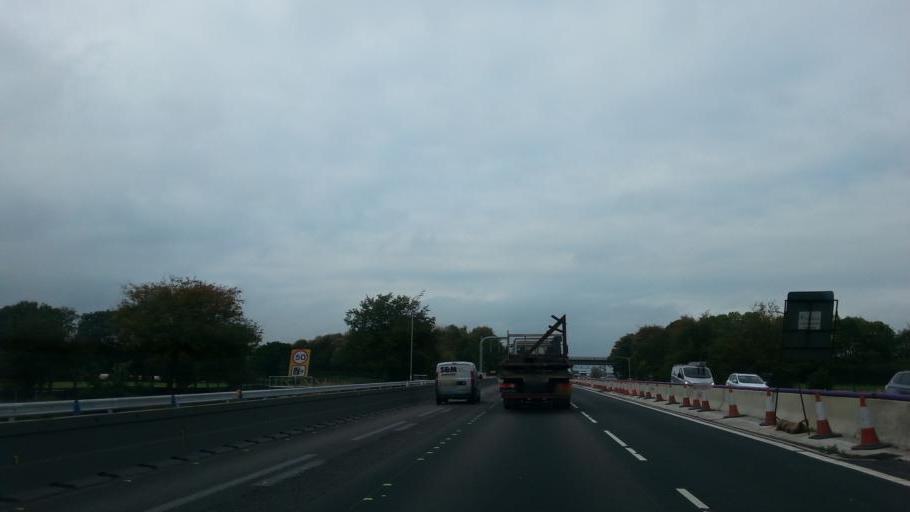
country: GB
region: England
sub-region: Cheshire East
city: Holmes Chapel
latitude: 53.1900
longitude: -2.3791
